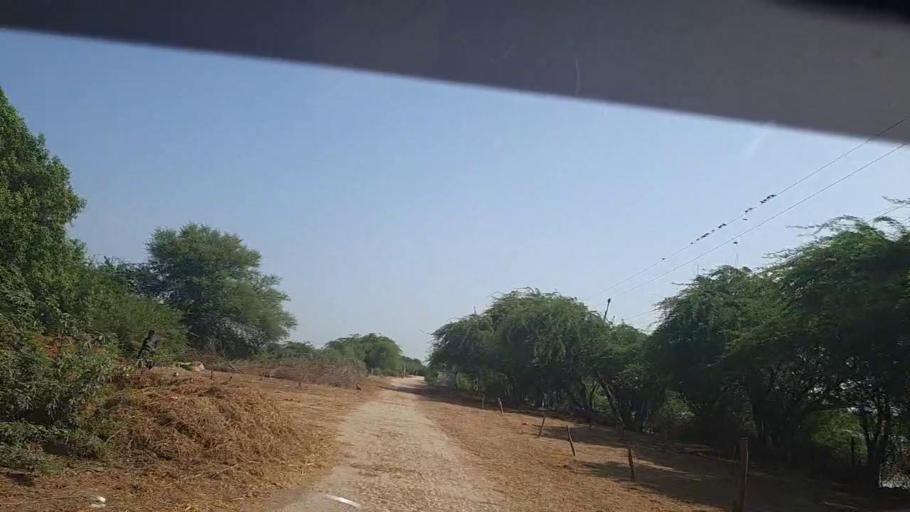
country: PK
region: Sindh
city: Rajo Khanani
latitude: 24.9652
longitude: 68.8899
